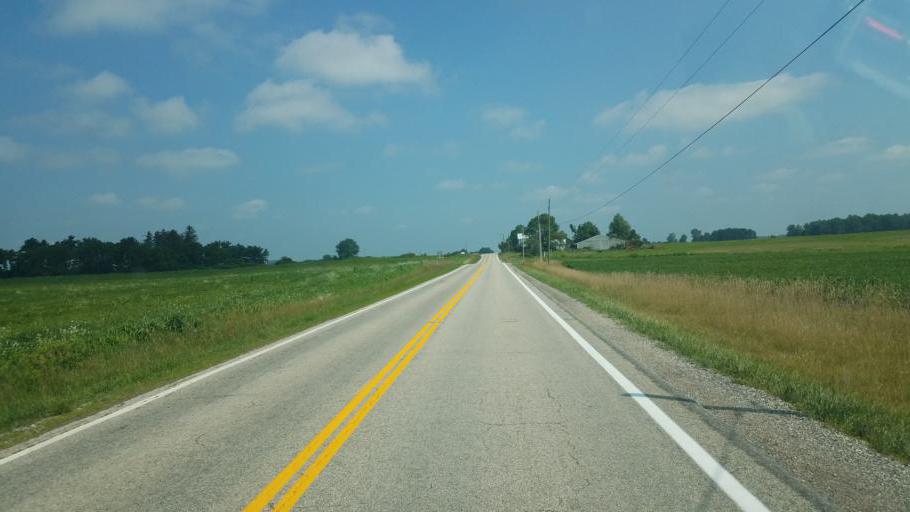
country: US
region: Ohio
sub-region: Crawford County
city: Bucyrus
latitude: 40.8936
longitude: -82.8548
